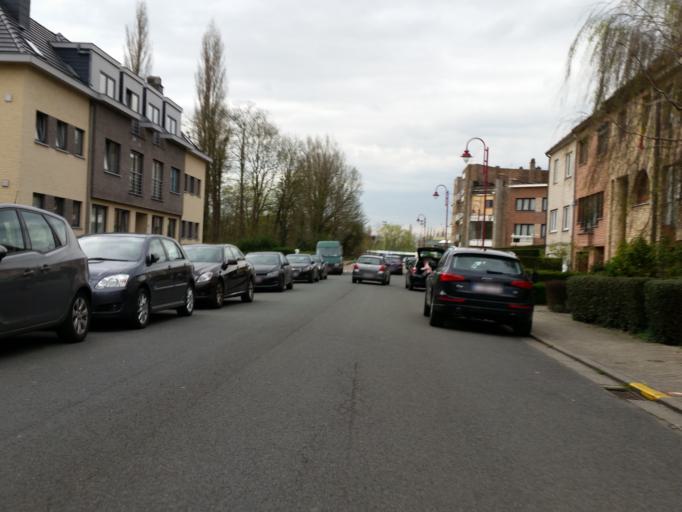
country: BE
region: Flanders
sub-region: Provincie Vlaams-Brabant
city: Dilbeek
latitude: 50.8673
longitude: 4.2872
